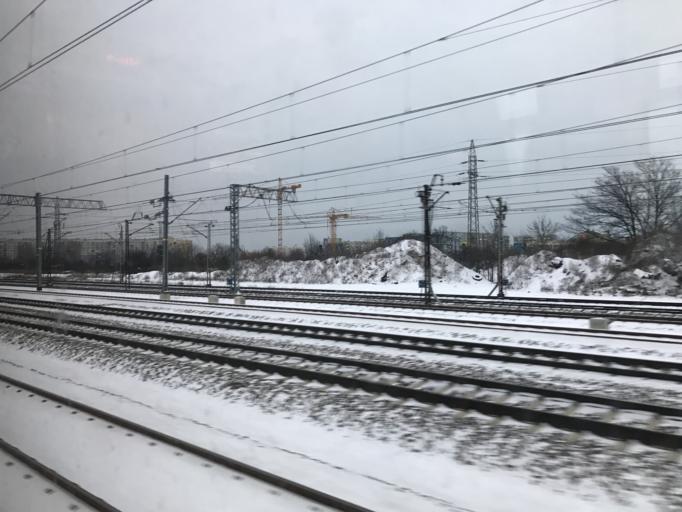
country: PL
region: Pomeranian Voivodeship
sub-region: Gdansk
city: Gdansk
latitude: 54.3859
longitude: 18.5981
